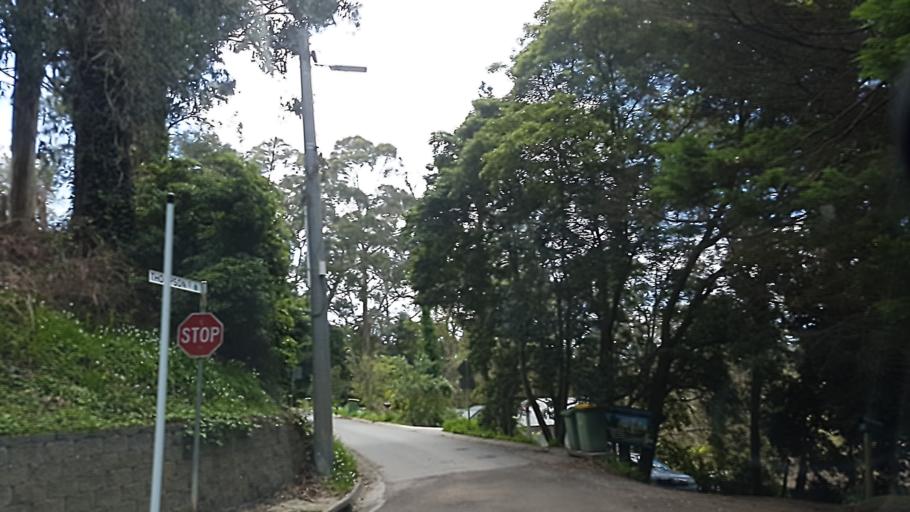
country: AU
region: Victoria
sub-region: Yarra Ranges
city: Tremont
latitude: -37.9104
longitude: 145.3340
